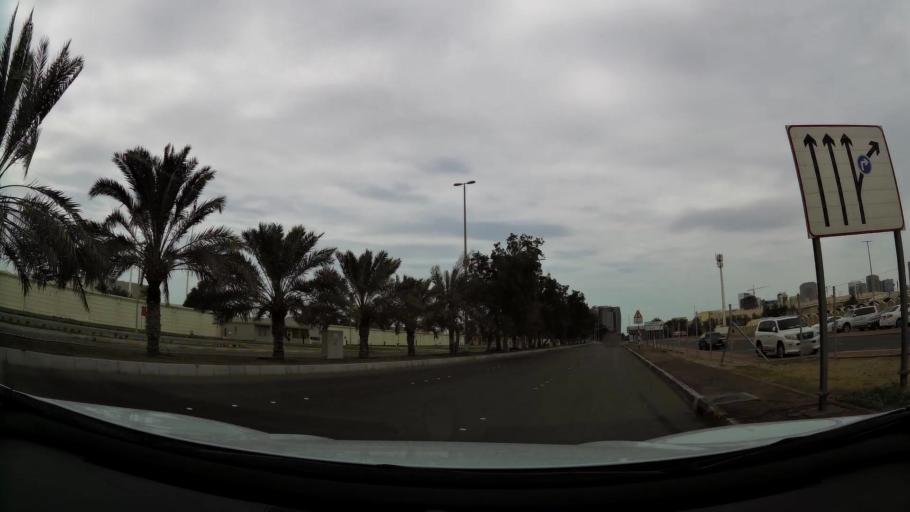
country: AE
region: Abu Dhabi
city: Abu Dhabi
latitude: 24.4214
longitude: 54.4277
